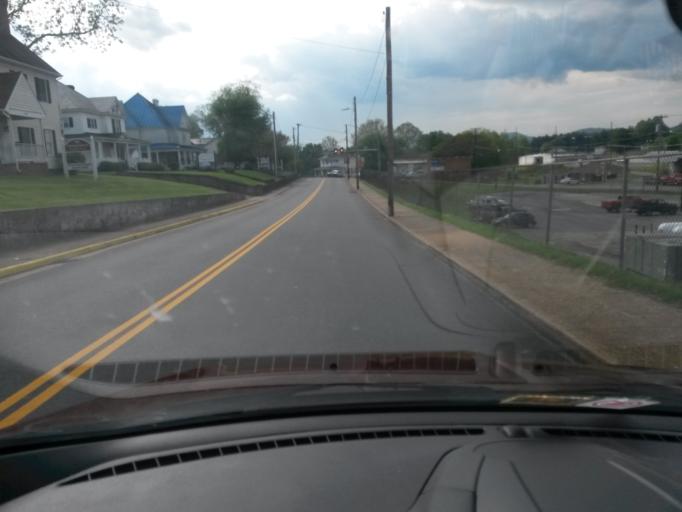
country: US
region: Virginia
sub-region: City of Bedford
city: Bedford
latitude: 37.3356
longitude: -79.5275
